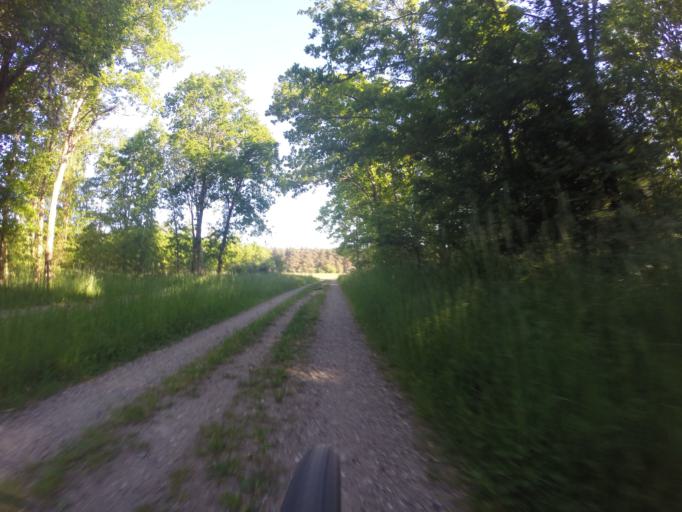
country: DK
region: Capital Region
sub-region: Ballerup Kommune
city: Ballerup
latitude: 55.6996
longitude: 12.3478
